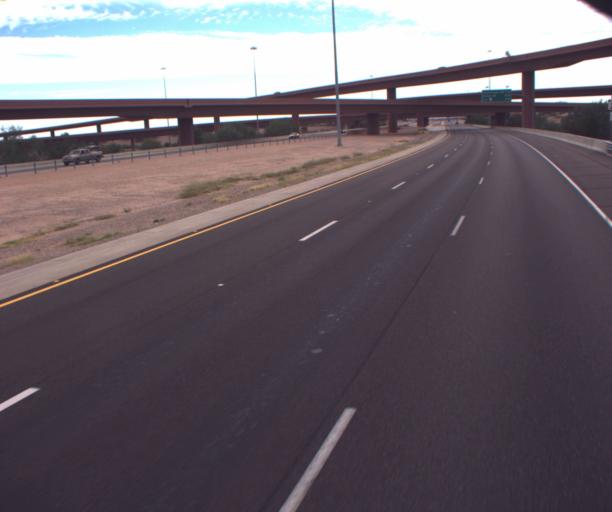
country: US
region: Arizona
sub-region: Pinal County
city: Apache Junction
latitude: 33.3893
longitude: -111.6480
